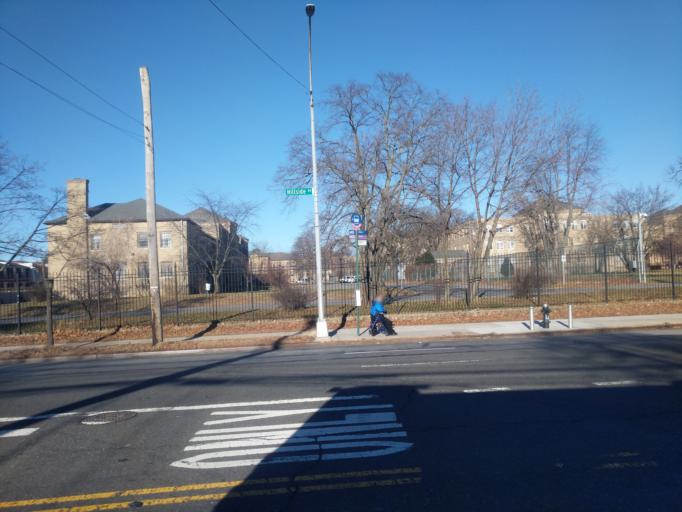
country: US
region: New York
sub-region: Nassau County
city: Bellerose Terrace
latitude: 40.7331
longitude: -73.7331
